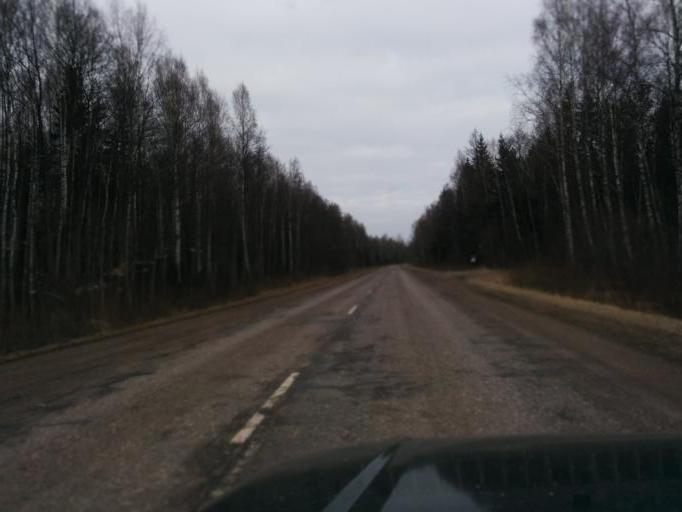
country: LV
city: Tireli
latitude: 56.8537
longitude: 23.5369
